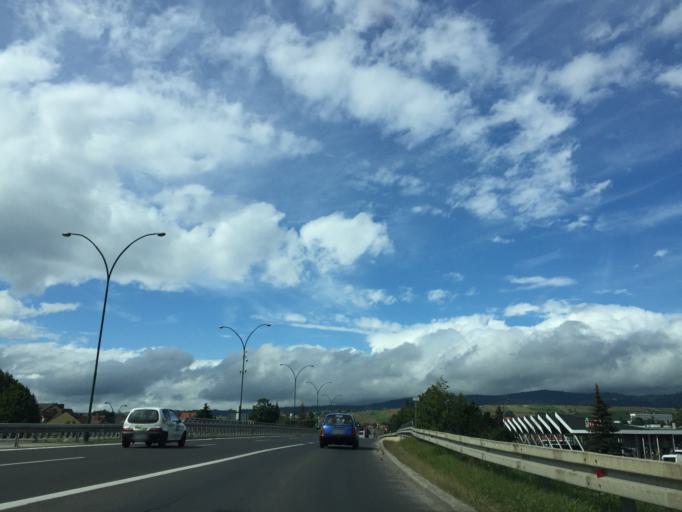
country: PL
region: Lesser Poland Voivodeship
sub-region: Powiat nowotarski
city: Nowy Targ
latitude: 49.4765
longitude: 20.0226
